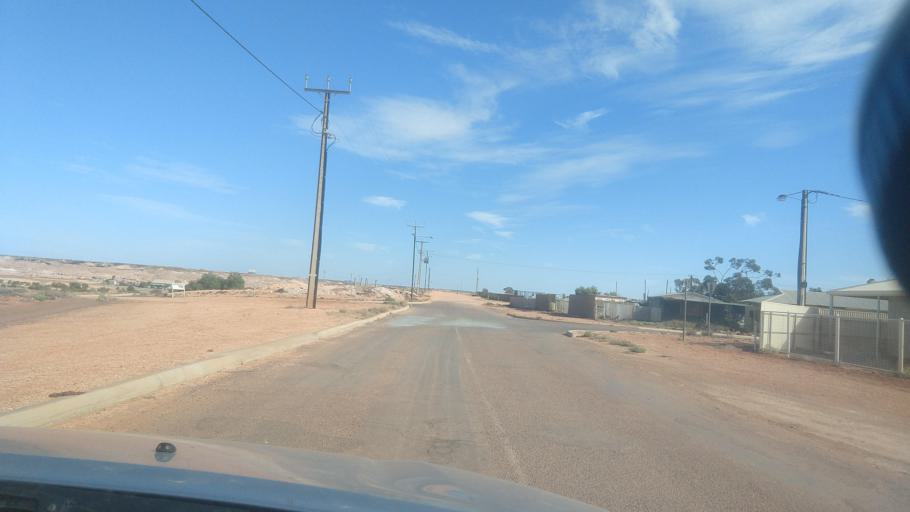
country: AU
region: South Australia
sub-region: Coober Pedy
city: Coober Pedy
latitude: -29.0134
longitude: 134.7503
